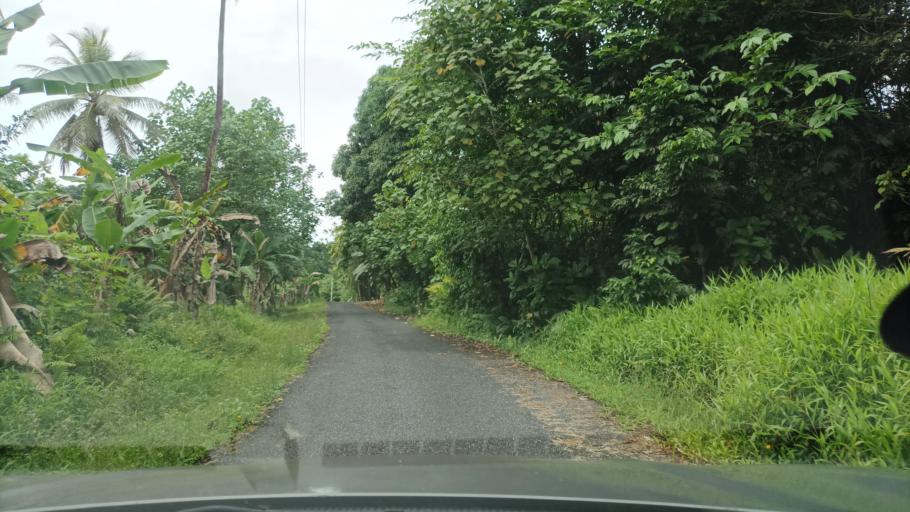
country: FM
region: Pohnpei
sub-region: Madolenihm Municipality
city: Madolenihm Municipality Government
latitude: 6.9142
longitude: 158.2890
